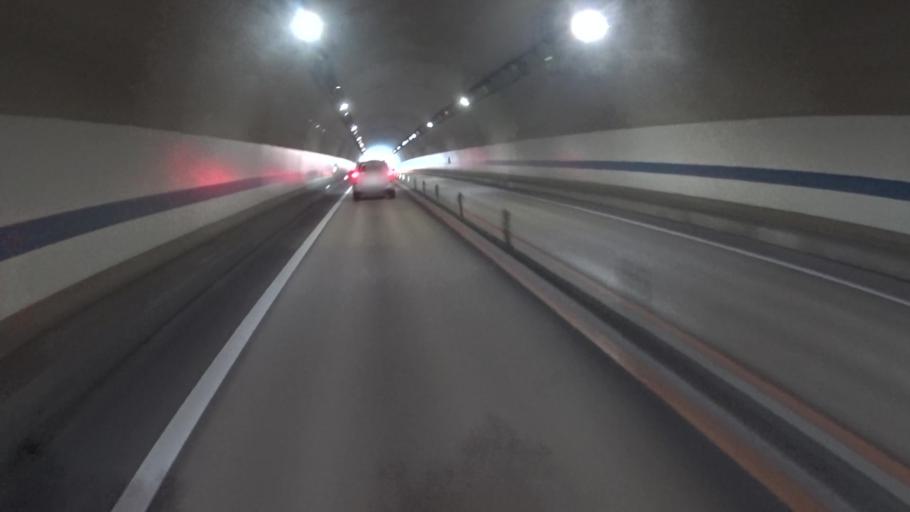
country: JP
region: Kyoto
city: Ayabe
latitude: 35.3781
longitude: 135.2604
